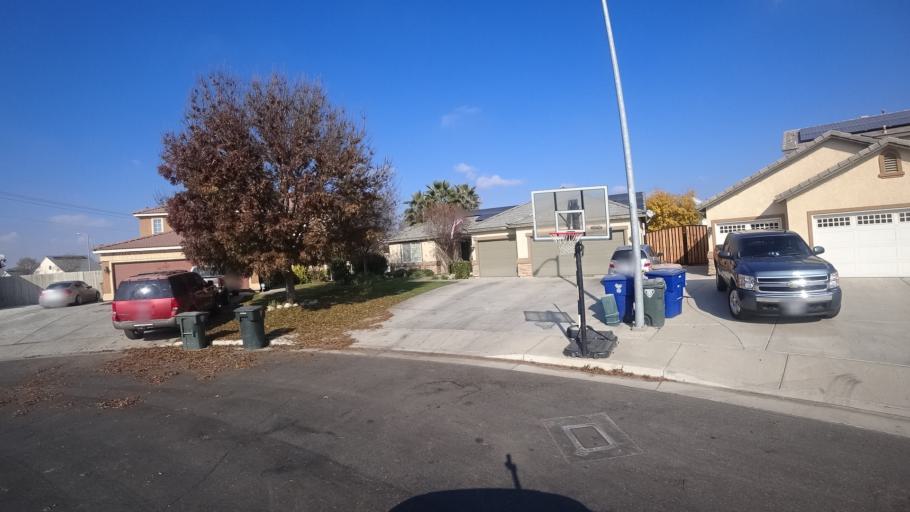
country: US
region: California
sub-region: Kern County
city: Greenacres
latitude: 35.3019
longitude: -119.1091
